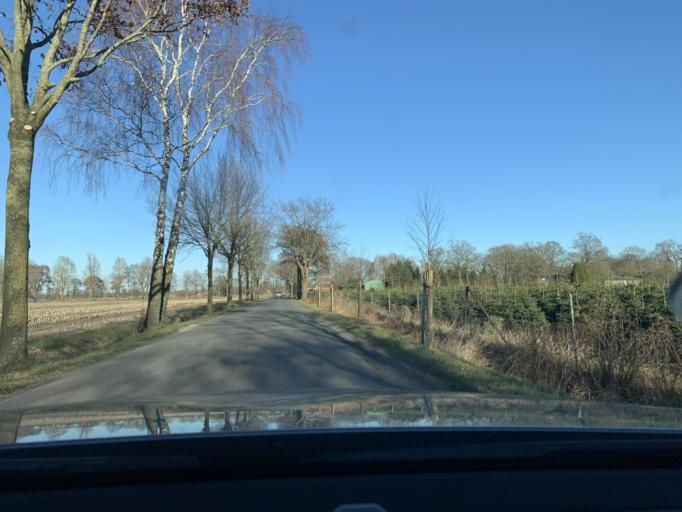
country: DE
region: Lower Saxony
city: Hatten
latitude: 53.0684
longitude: 8.3002
